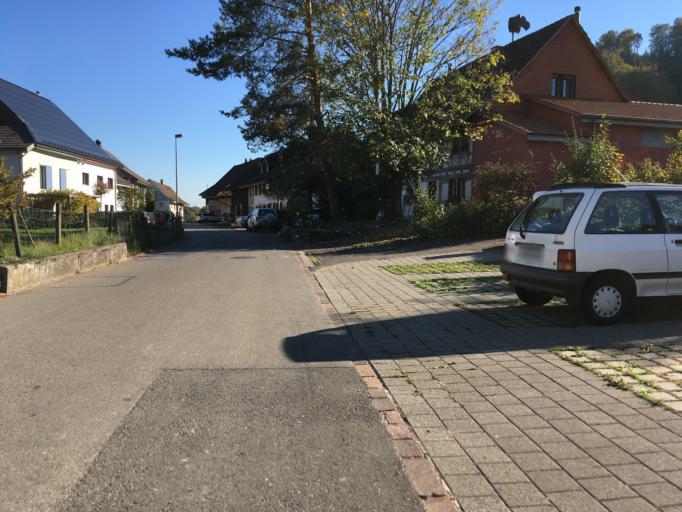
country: CH
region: Zurich
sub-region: Bezirk Buelach
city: Seglingen
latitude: 47.5649
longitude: 8.5442
